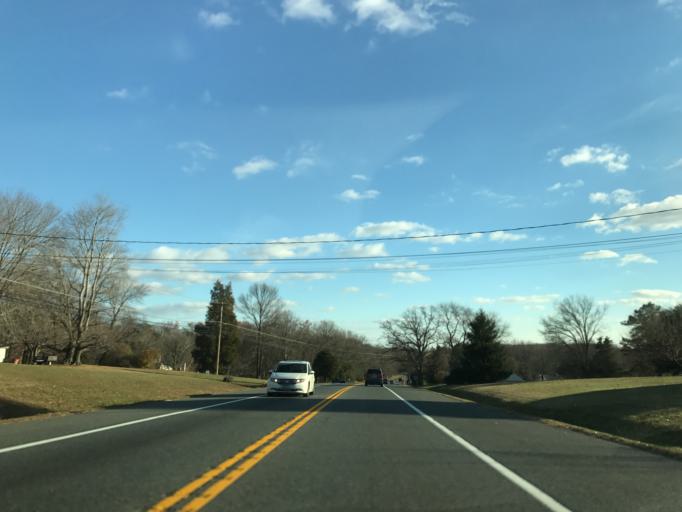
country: US
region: Maryland
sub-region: Harford County
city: Joppatowne
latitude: 39.4549
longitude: -76.3576
